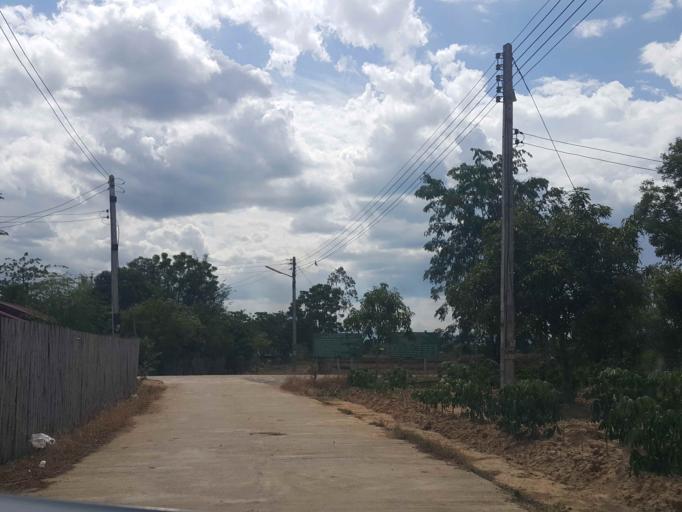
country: TH
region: Sukhothai
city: Thung Saliam
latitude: 17.3280
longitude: 99.4397
